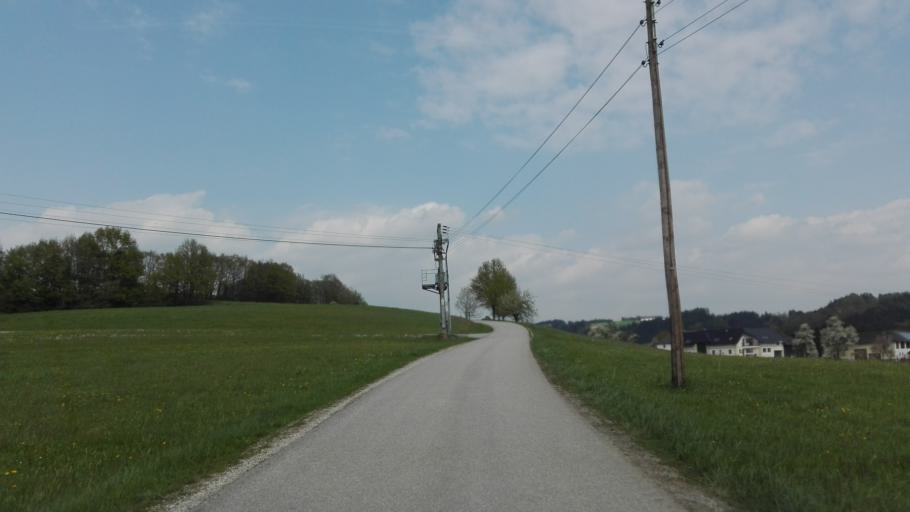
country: AT
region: Upper Austria
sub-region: Politischer Bezirk Perg
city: Bad Kreuzen
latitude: 48.2349
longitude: 14.7358
